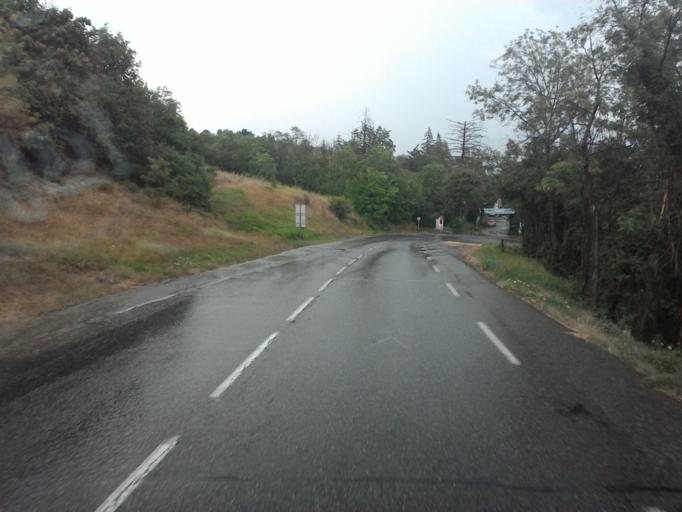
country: FR
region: Provence-Alpes-Cote d'Azur
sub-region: Departement des Hautes-Alpes
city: Gap
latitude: 44.5824
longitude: 6.0811
